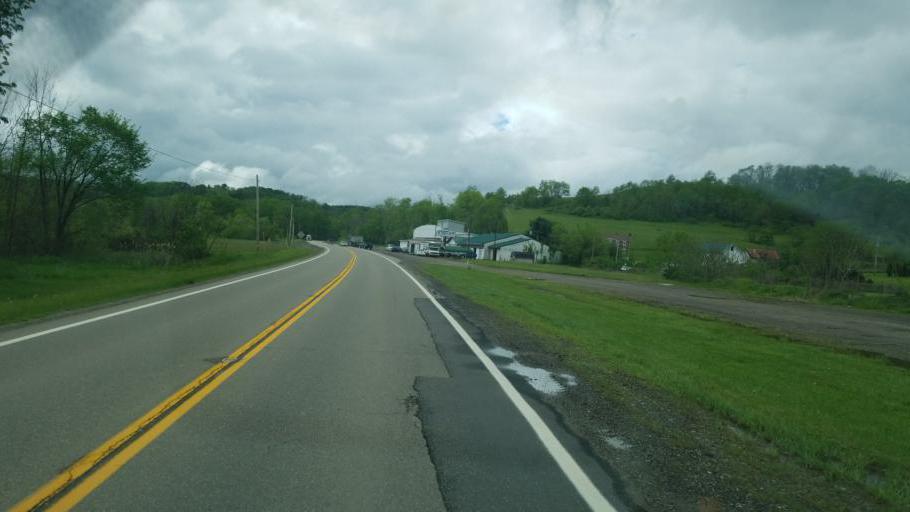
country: US
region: Ohio
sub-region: Harrison County
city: Cadiz
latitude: 40.3116
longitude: -81.1069
